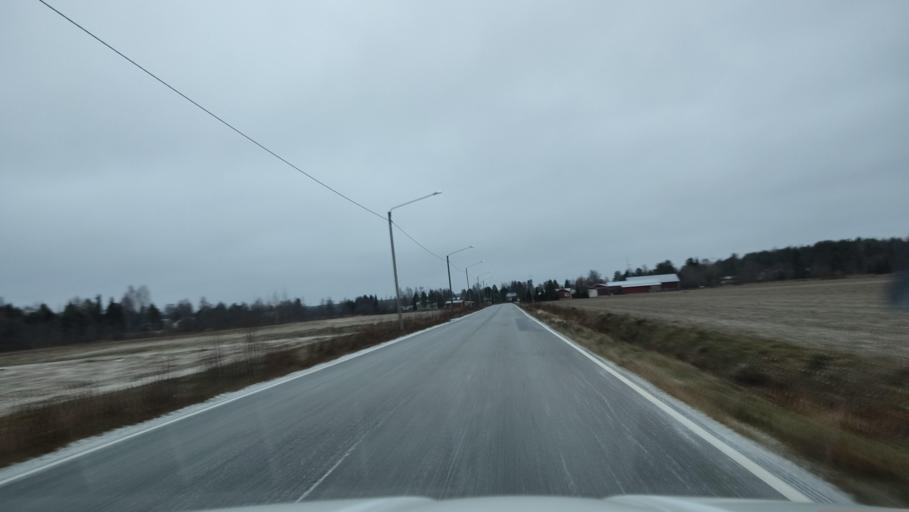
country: FI
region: Southern Ostrobothnia
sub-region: Suupohja
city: Karijoki
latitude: 62.2366
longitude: 21.6549
